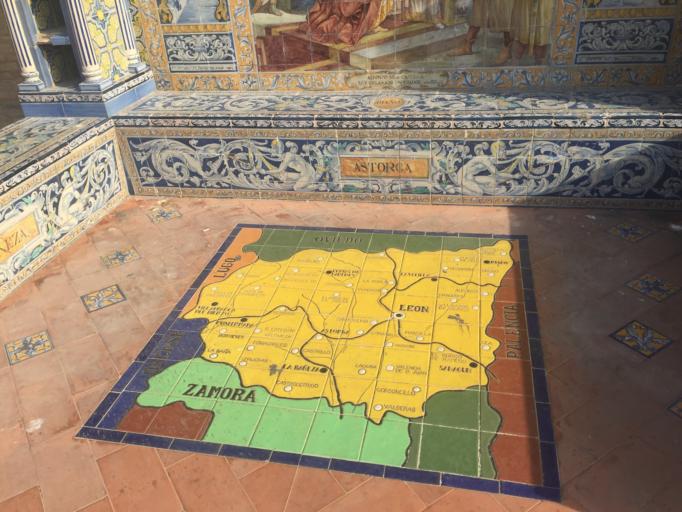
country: ES
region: Andalusia
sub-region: Provincia de Sevilla
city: Sevilla
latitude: 37.3770
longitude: -5.9859
